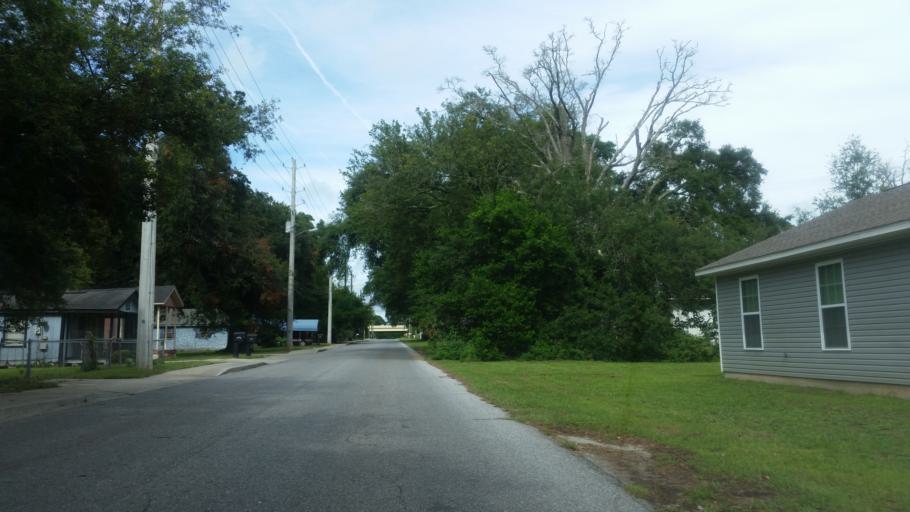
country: US
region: Florida
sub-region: Escambia County
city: Goulding
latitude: 30.4395
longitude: -87.2199
